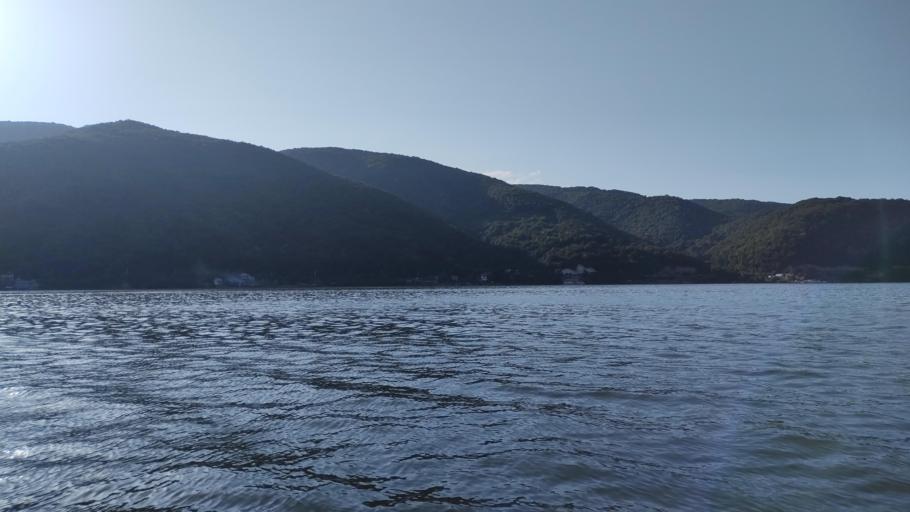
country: RO
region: Mehedinti
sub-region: Comuna Dubova
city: Dubova
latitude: 44.5725
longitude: 22.2424
